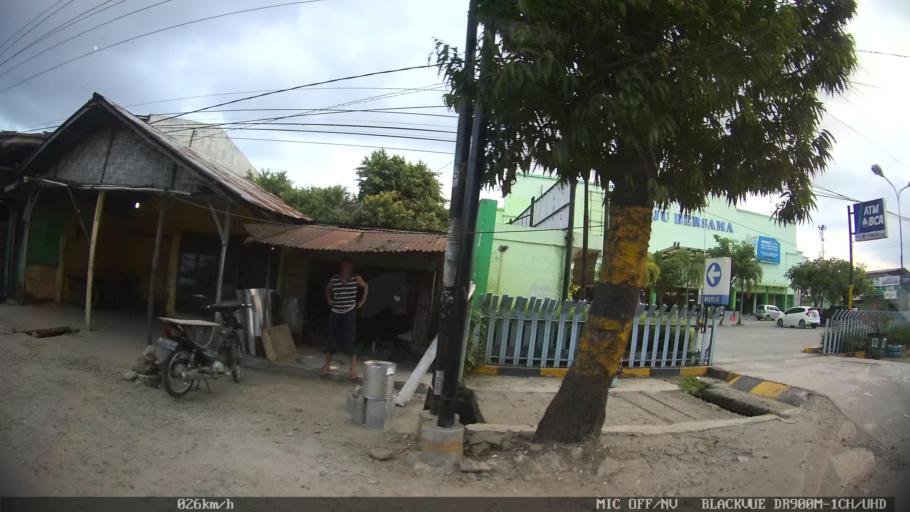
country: ID
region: North Sumatra
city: Medan
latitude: 3.5975
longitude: 98.7289
